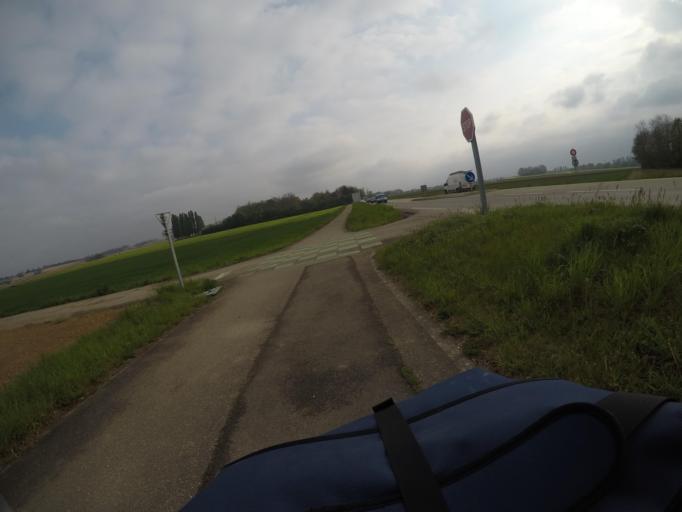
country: FR
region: Alsace
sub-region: Departement du Bas-Rhin
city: Wolfisheim
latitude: 48.5952
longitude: 7.6732
